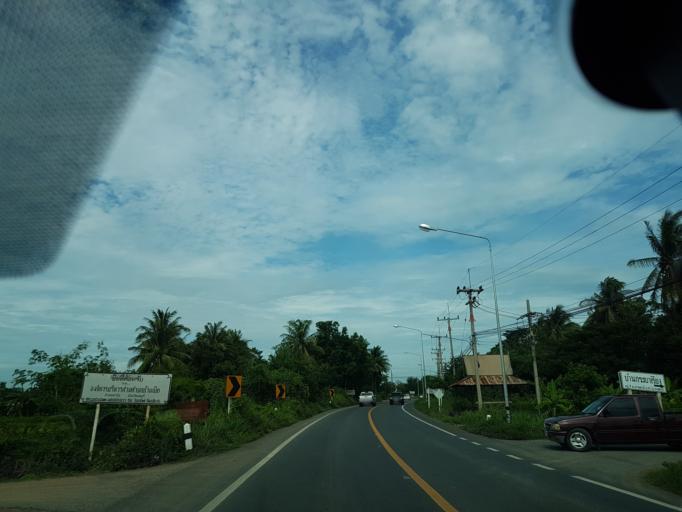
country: TH
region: Ang Thong
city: Chaiyo
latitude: 14.7331
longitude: 100.5162
